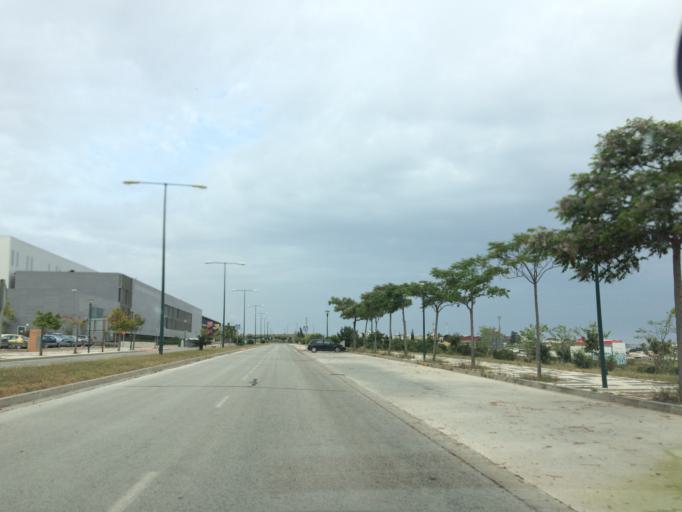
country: ES
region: Andalusia
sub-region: Provincia de Malaga
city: Malaga
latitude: 36.7148
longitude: -4.4979
